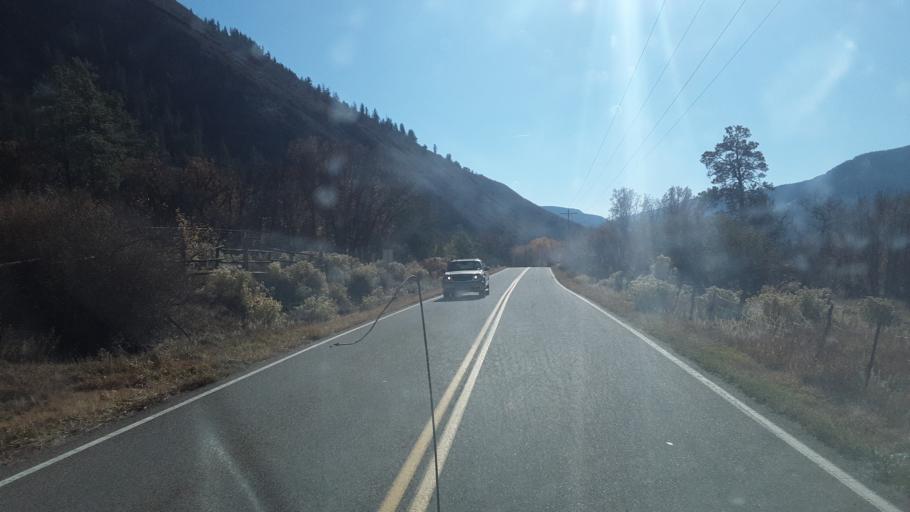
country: US
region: Colorado
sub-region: La Plata County
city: Durango
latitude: 37.3954
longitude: -107.8232
